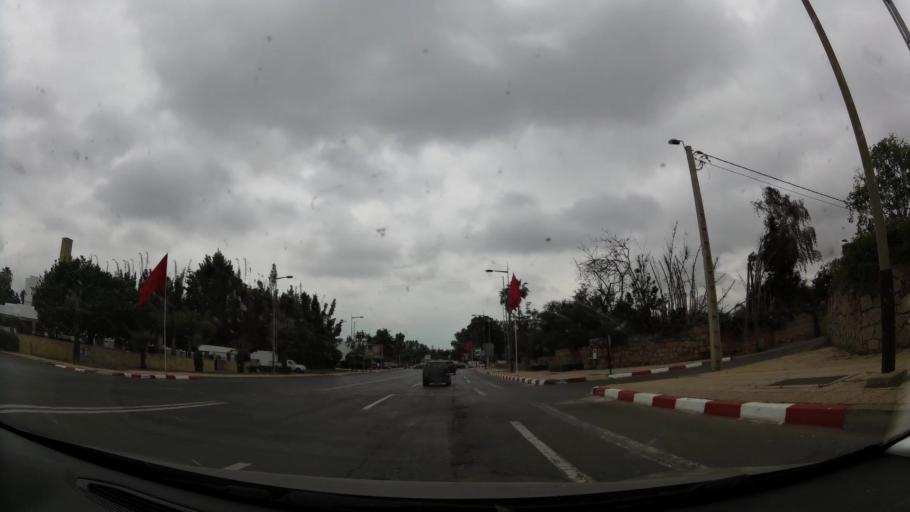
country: MA
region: Rabat-Sale-Zemmour-Zaer
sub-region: Rabat
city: Rabat
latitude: 33.9724
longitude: -6.8294
